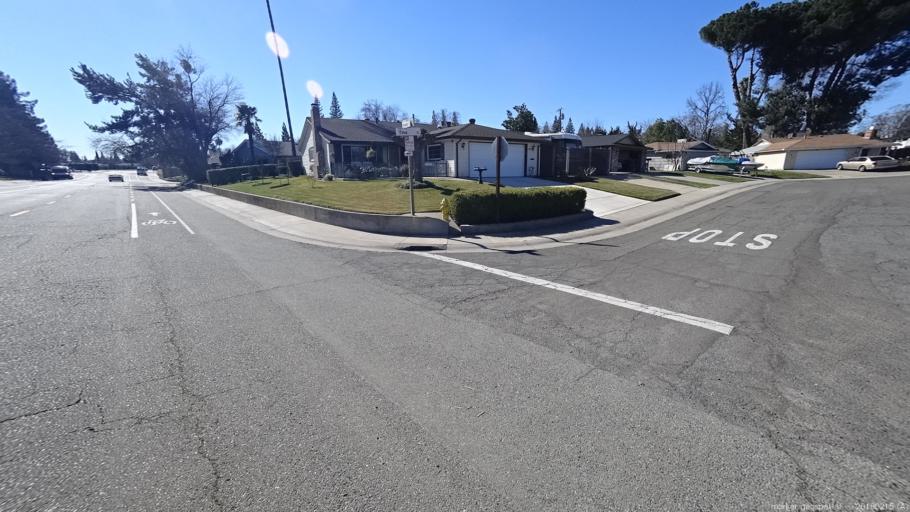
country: US
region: California
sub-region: Sacramento County
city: Foothill Farms
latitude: 38.6694
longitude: -121.3159
